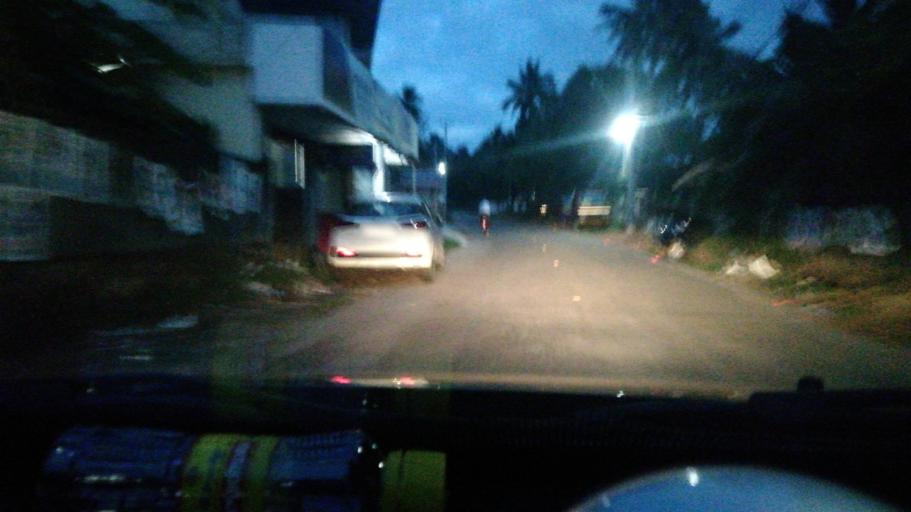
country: IN
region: Kerala
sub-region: Thiruvananthapuram
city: Paravur
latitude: 8.8120
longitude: 76.6817
